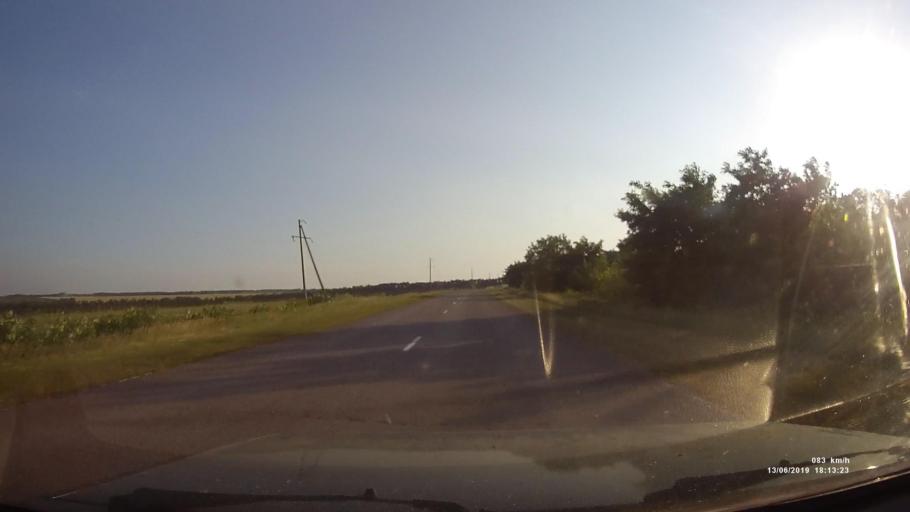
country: RU
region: Rostov
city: Kazanskaya
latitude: 49.9392
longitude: 41.3954
